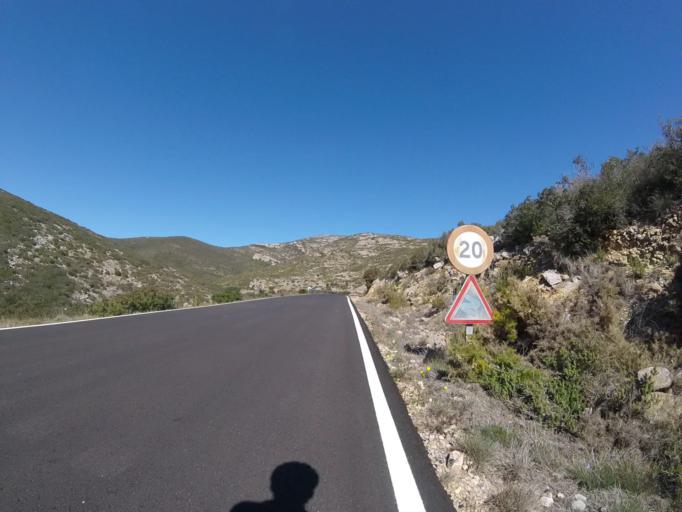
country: ES
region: Valencia
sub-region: Provincia de Castello
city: Alcoceber
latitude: 40.2338
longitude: 0.2696
